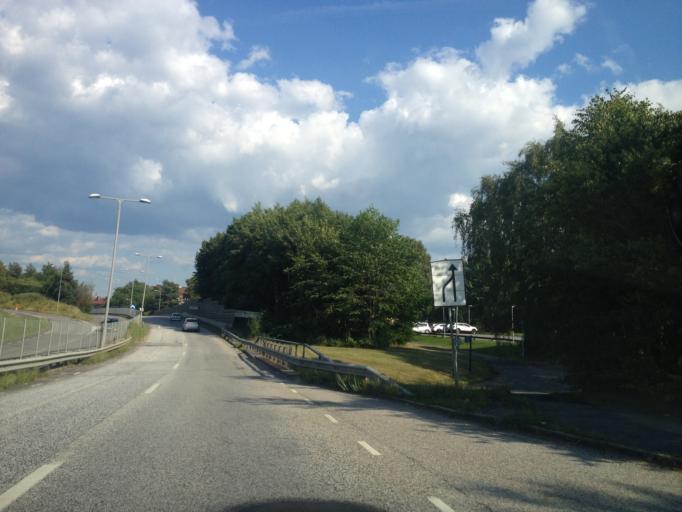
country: SE
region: Vaestra Goetaland
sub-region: Goteborg
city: Majorna
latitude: 57.6751
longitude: 11.9191
